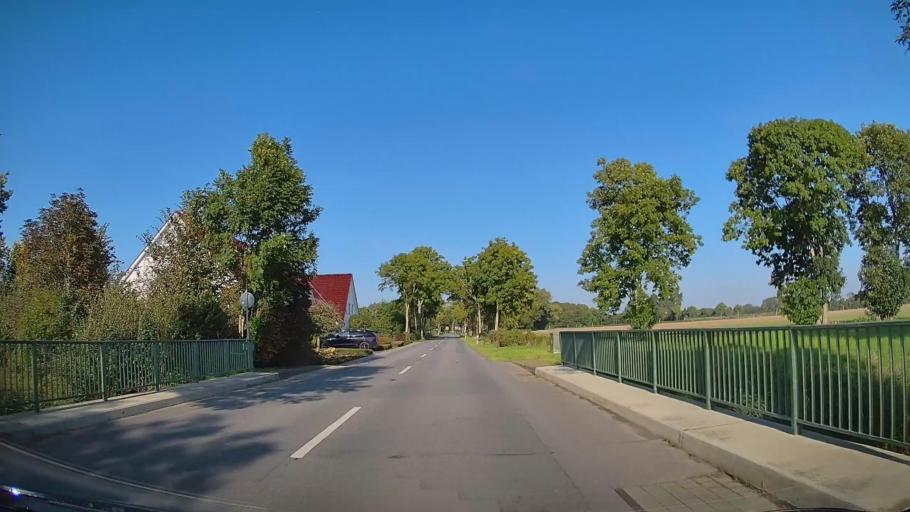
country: DE
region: Lower Saxony
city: Cappel
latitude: 53.7486
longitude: 8.5600
